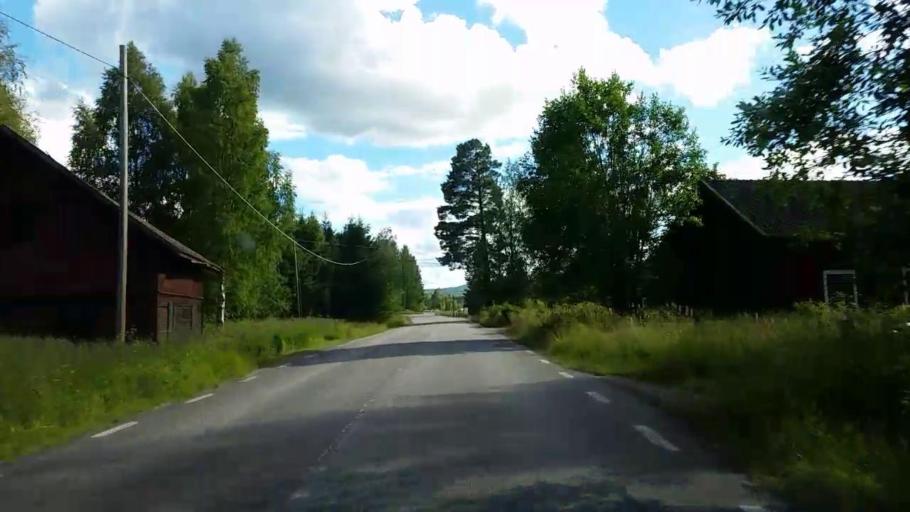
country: SE
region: Vaesternorrland
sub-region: Ange Kommun
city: Ange
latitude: 62.1639
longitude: 15.6786
